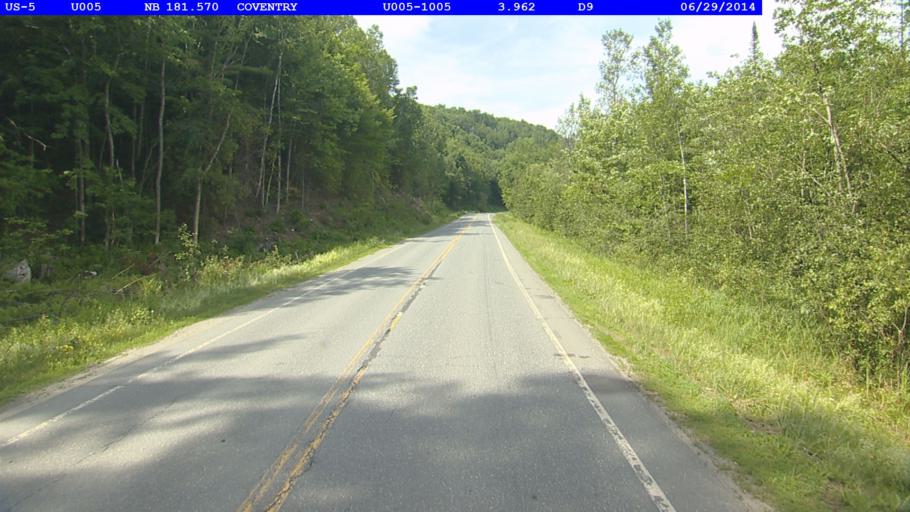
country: US
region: Vermont
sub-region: Orleans County
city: Newport
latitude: 44.9118
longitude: -72.2391
